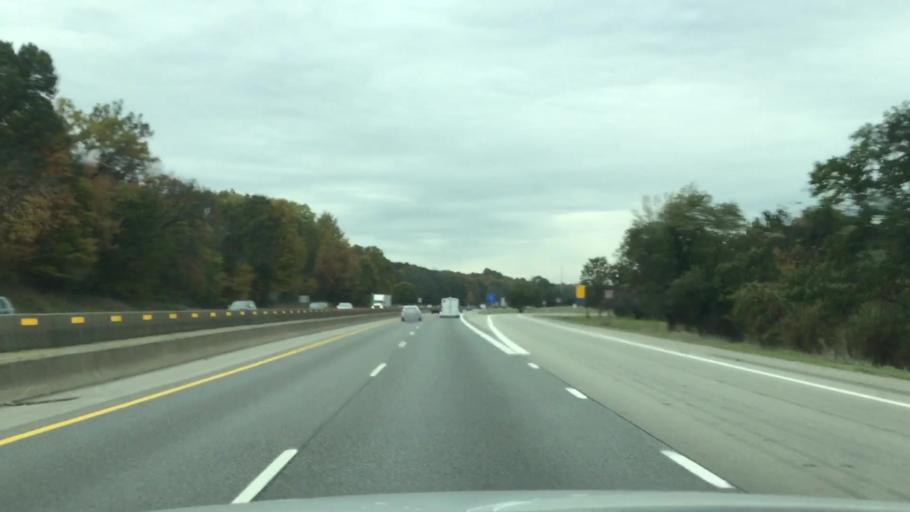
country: US
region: Michigan
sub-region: Kalamazoo County
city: Galesburg
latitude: 42.2721
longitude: -85.4366
